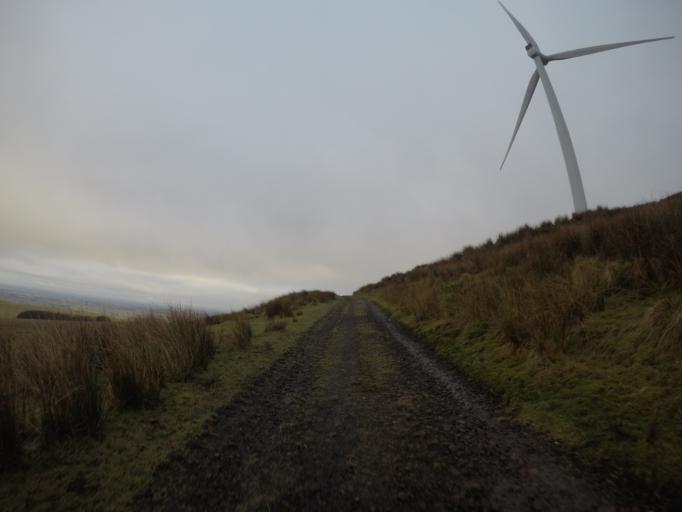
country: GB
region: Scotland
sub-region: North Ayrshire
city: Dalry
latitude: 55.7369
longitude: -4.7702
